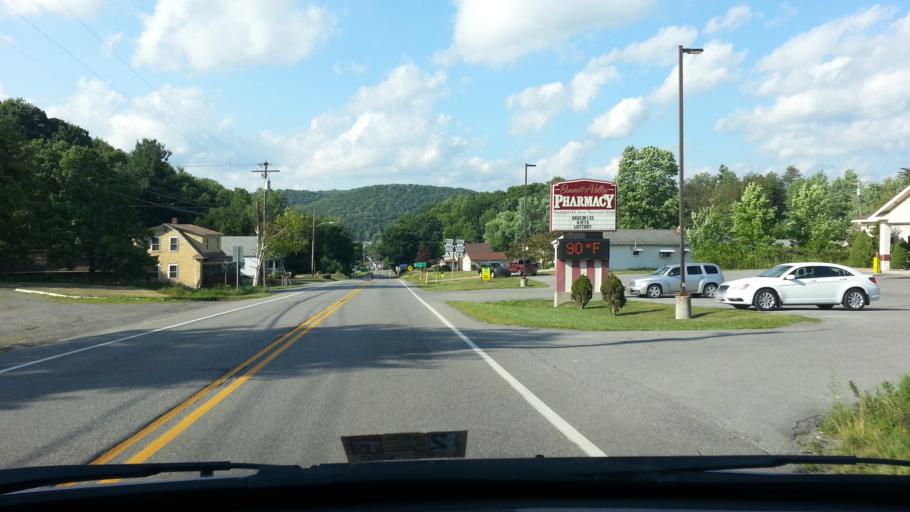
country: US
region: Pennsylvania
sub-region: Elk County
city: Saint Marys
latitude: 41.2678
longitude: -78.4971
